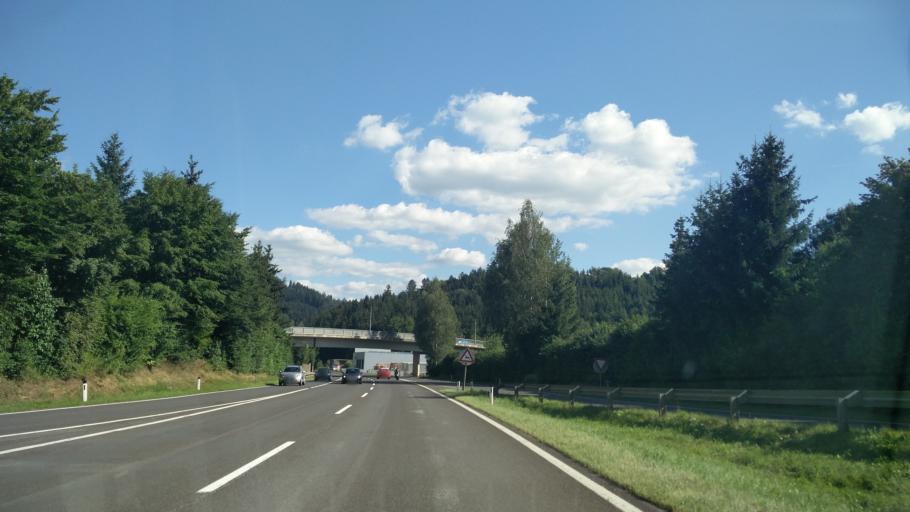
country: AT
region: Styria
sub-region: Politischer Bezirk Leoben
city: Trofaiach
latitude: 47.4219
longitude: 15.0007
